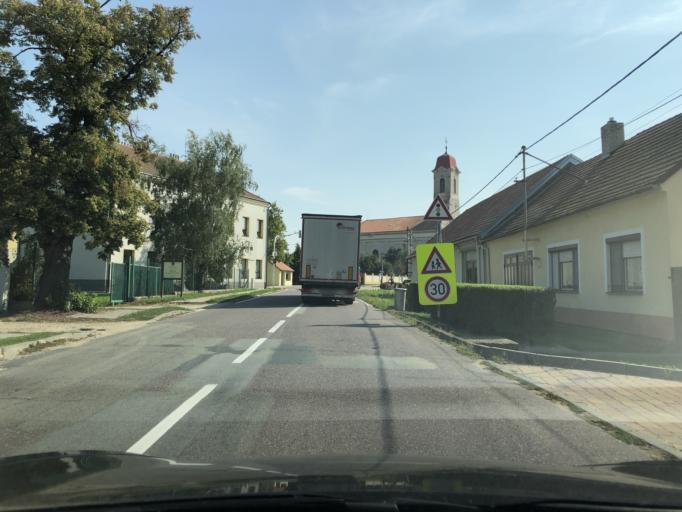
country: CZ
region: South Moravian
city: Brezi
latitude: 48.8216
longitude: 16.5620
